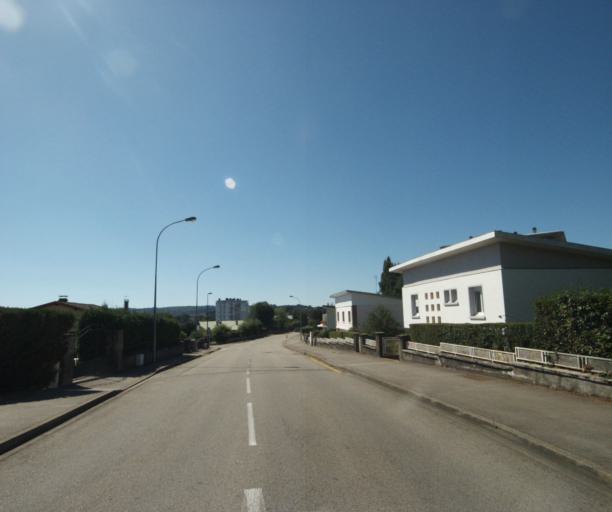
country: FR
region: Lorraine
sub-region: Departement des Vosges
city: Epinal
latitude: 48.1834
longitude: 6.4576
